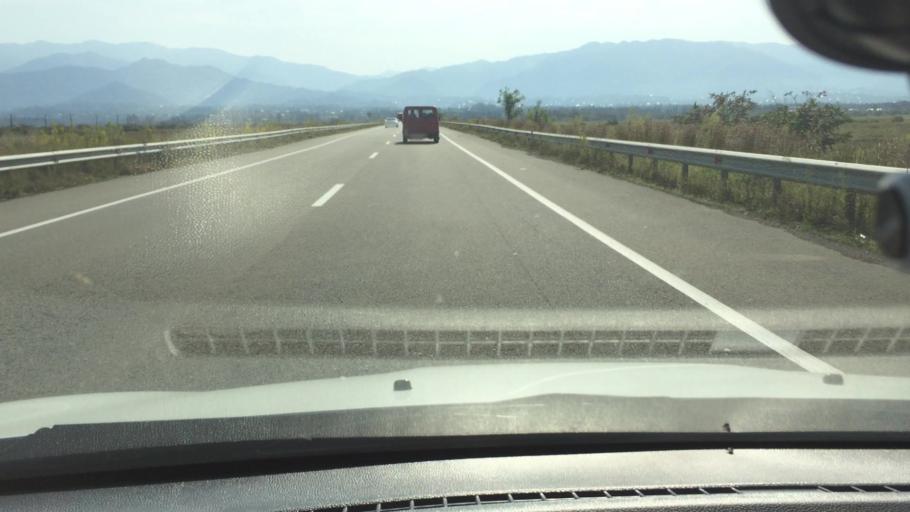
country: GE
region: Ajaria
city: Ochkhamuri
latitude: 41.8747
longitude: 41.8264
